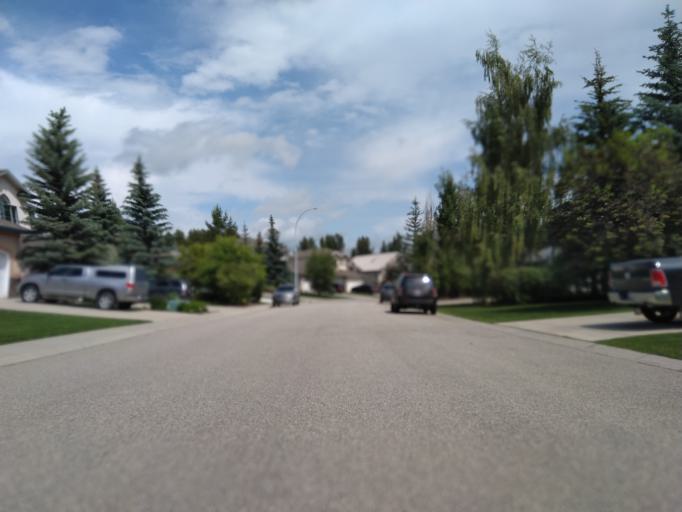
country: CA
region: Alberta
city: Cochrane
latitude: 51.1871
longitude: -114.4993
